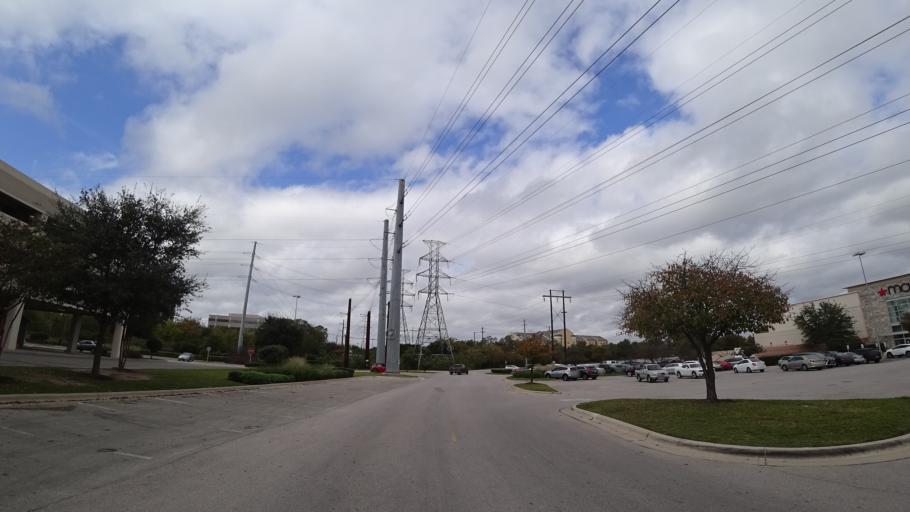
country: US
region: Texas
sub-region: Williamson County
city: Jollyville
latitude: 30.3984
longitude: -97.7272
